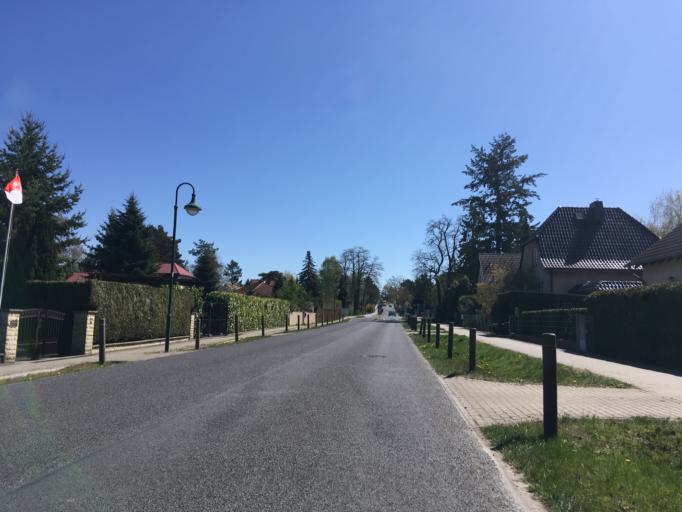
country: DE
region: Brandenburg
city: Bernau bei Berlin
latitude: 52.6464
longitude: 13.5526
